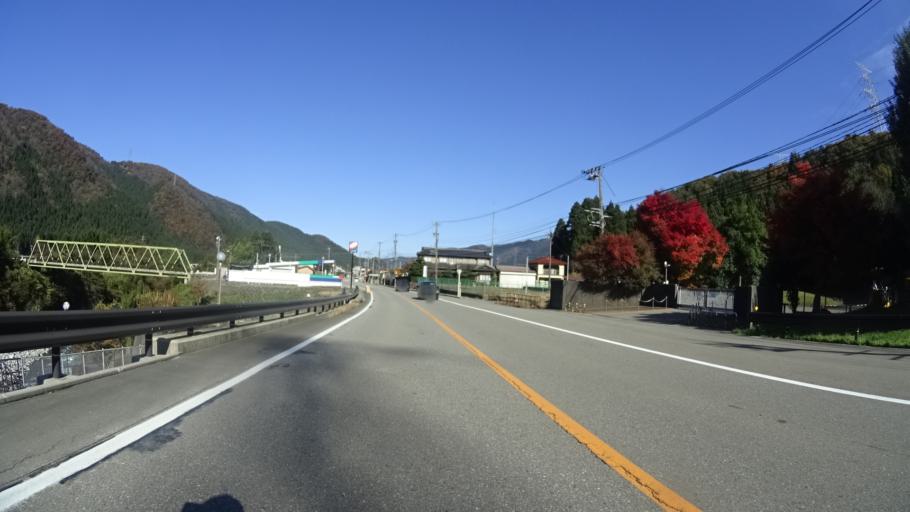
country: JP
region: Ishikawa
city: Tsurugi-asahimachi
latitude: 36.4103
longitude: 136.6324
